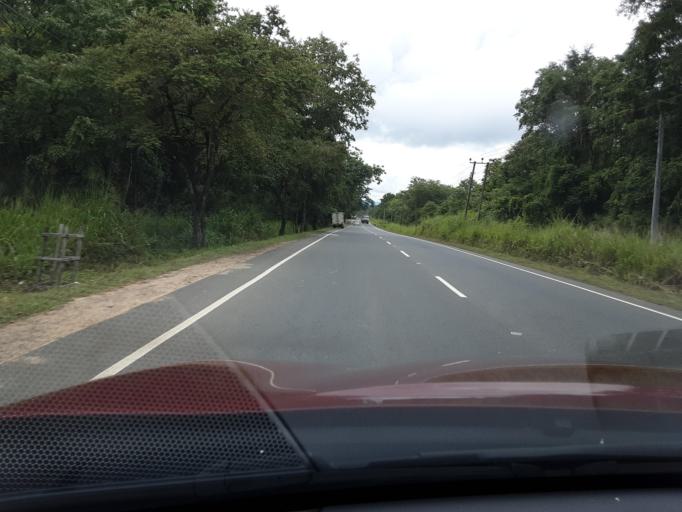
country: LK
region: Uva
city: Badulla
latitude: 7.3980
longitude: 81.1112
